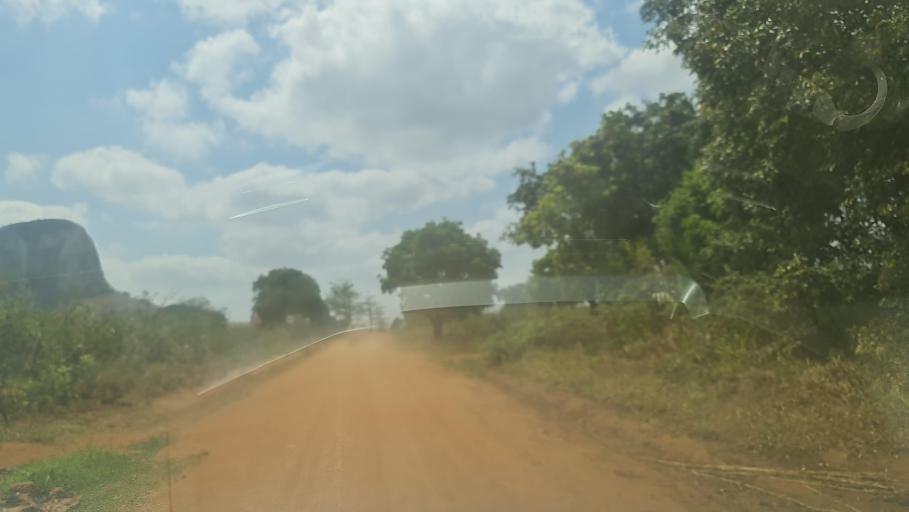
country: MW
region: Southern Region
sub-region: Nsanje District
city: Nsanje
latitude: -17.3953
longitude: 35.5708
